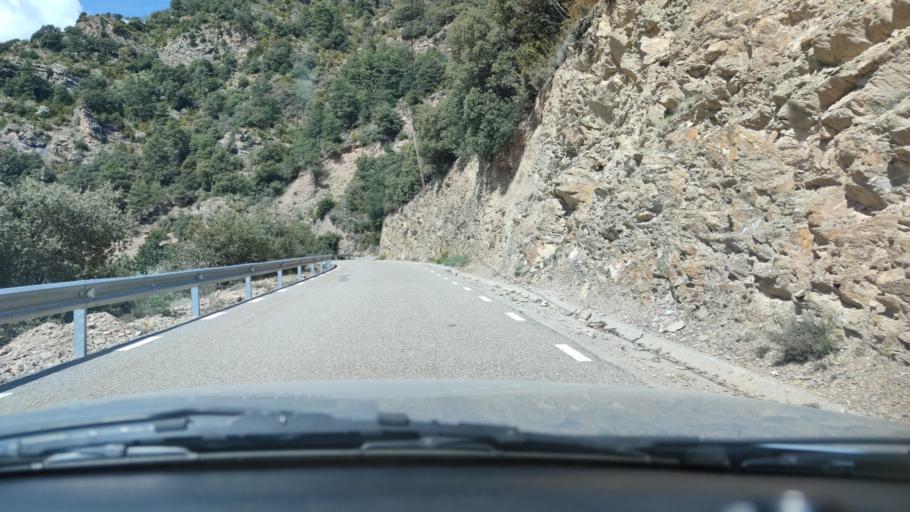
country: ES
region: Catalonia
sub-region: Provincia de Lleida
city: Coll de Nargo
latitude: 42.2941
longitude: 1.2669
